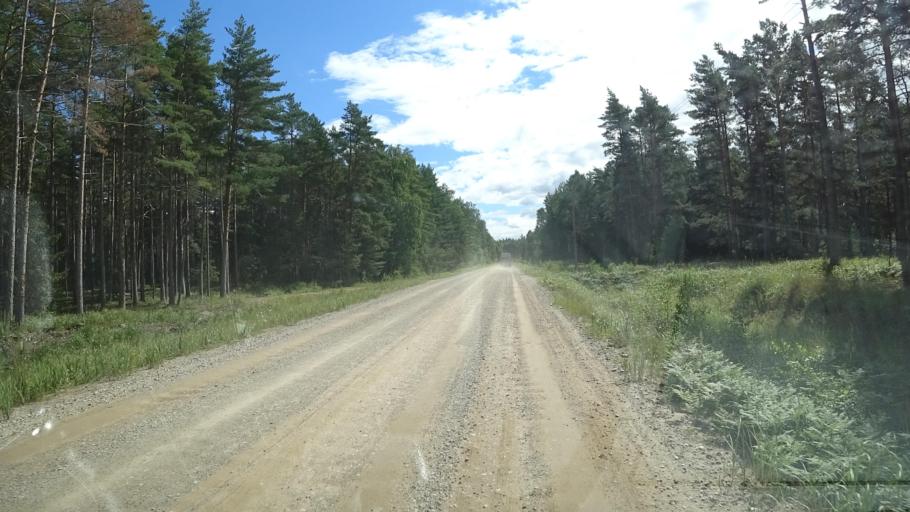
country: LV
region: Ventspils
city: Ventspils
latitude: 57.4884
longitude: 21.6693
